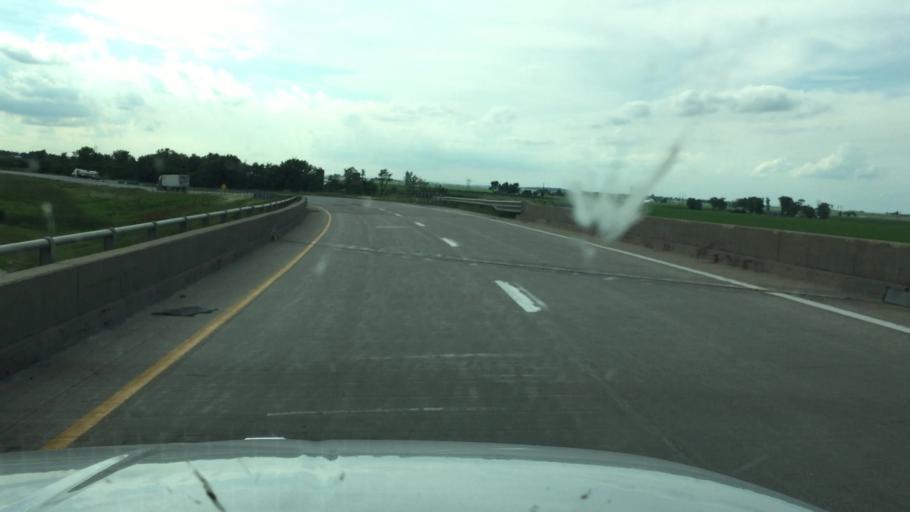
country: US
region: Iowa
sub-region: Scott County
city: Walcott
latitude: 41.6029
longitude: -90.6784
